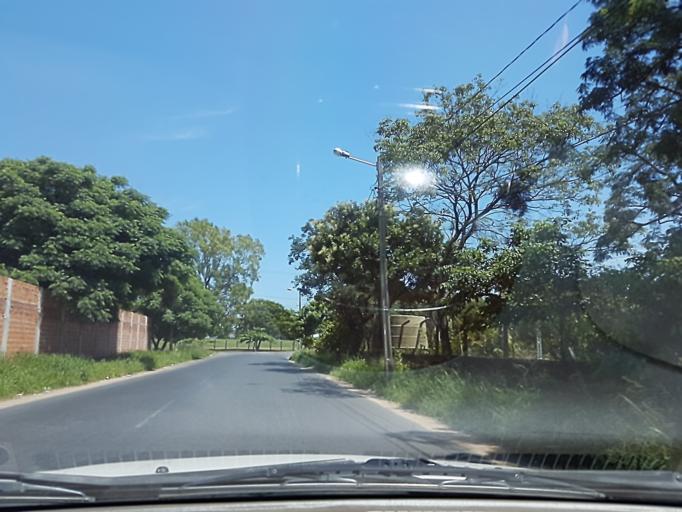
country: PY
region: Central
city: Fernando de la Mora
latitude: -25.2694
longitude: -57.5221
